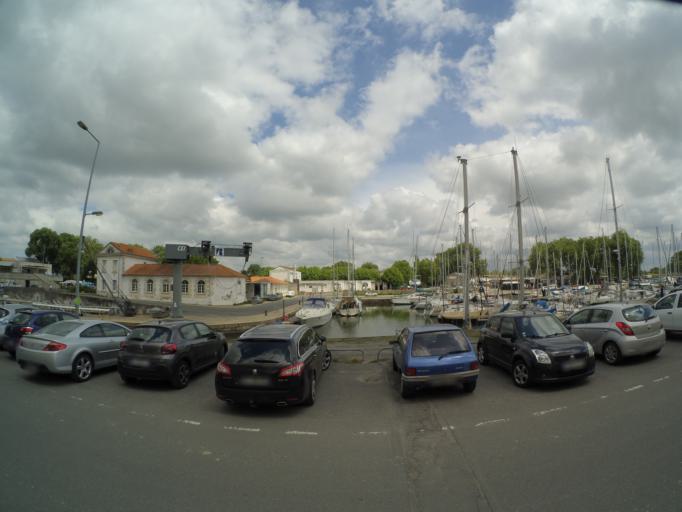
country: FR
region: Poitou-Charentes
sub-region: Departement de la Charente-Maritime
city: Rochefort
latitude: 45.9433
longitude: -0.9577
